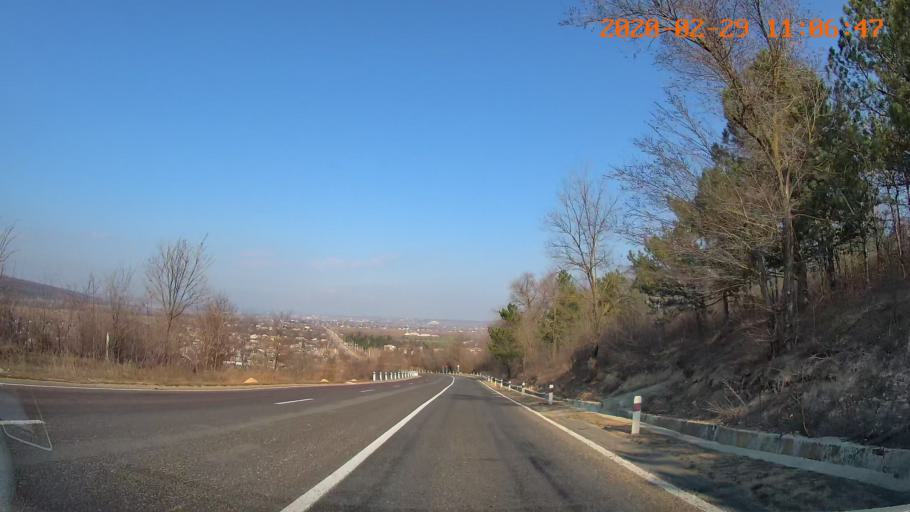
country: MD
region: Criuleni
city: Criuleni
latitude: 47.2184
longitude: 29.1867
